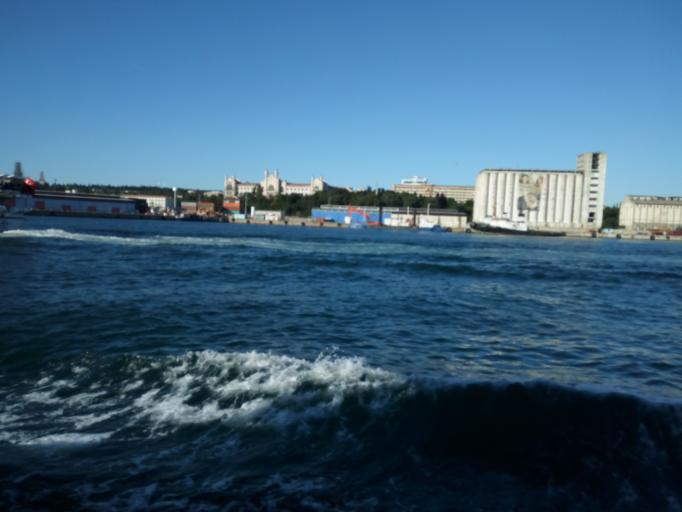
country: TR
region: Istanbul
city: UEskuedar
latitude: 40.9983
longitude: 29.0134
